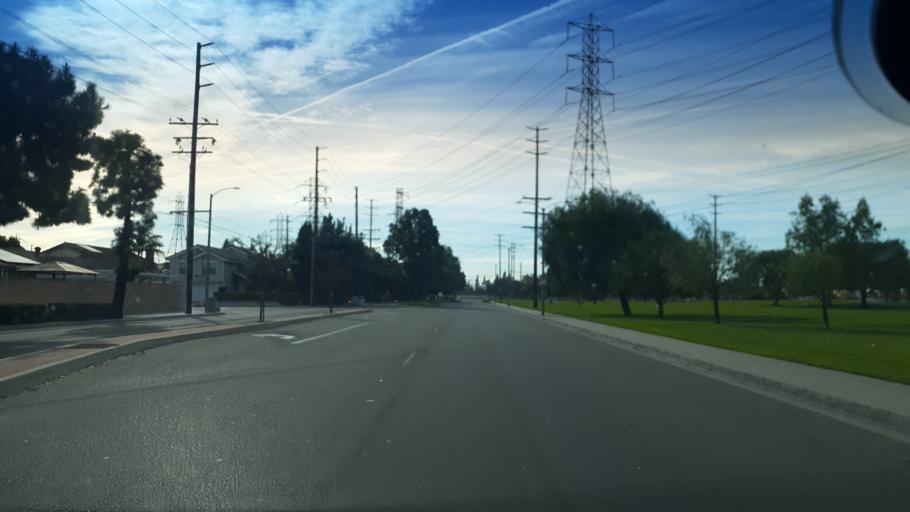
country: US
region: California
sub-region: Los Angeles County
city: Artesia
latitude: 33.8528
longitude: -118.0996
